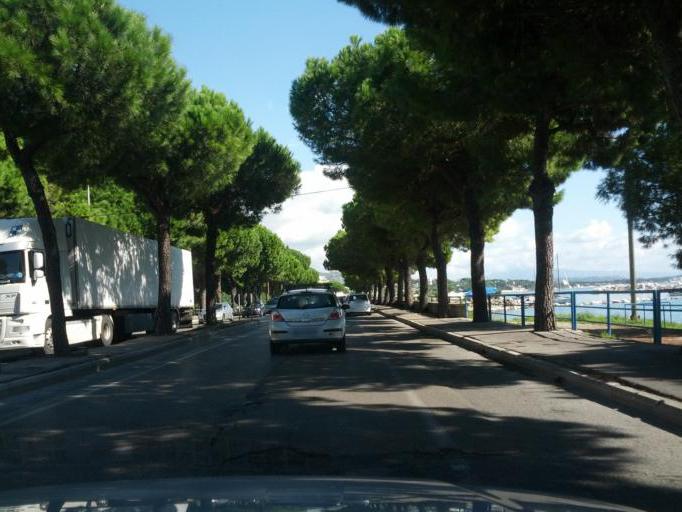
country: IT
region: Latium
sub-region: Provincia di Latina
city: Formia
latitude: 41.2576
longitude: 13.6121
